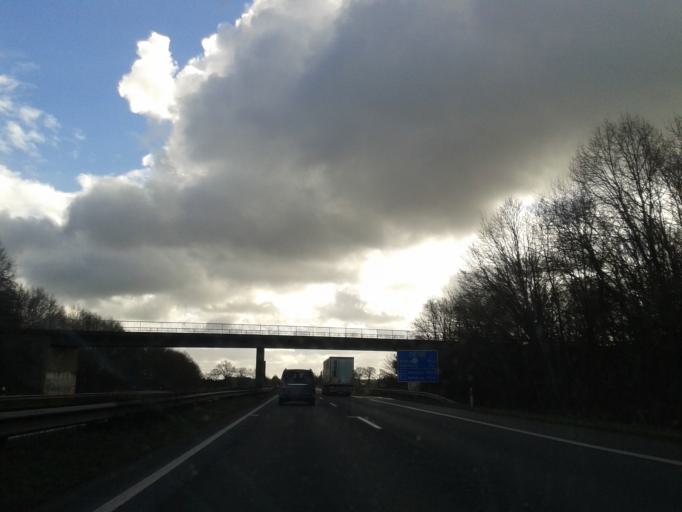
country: DE
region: Lower Saxony
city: Wiefelstede
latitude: 53.1820
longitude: 8.1095
